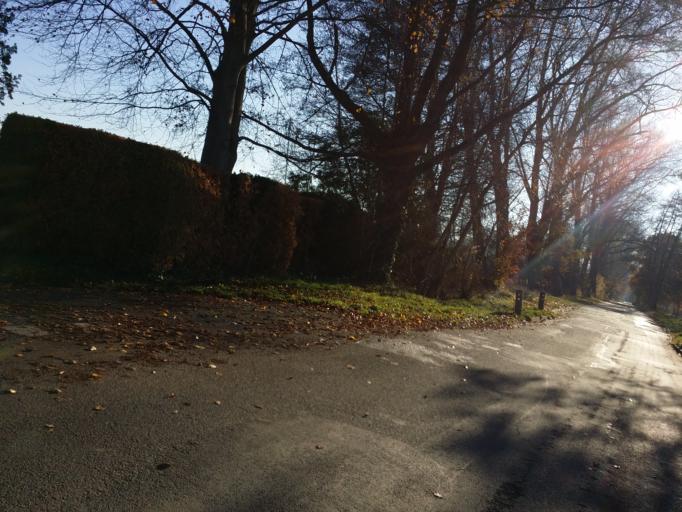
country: DE
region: Lower Saxony
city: Oyten
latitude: 53.0746
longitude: 8.9673
